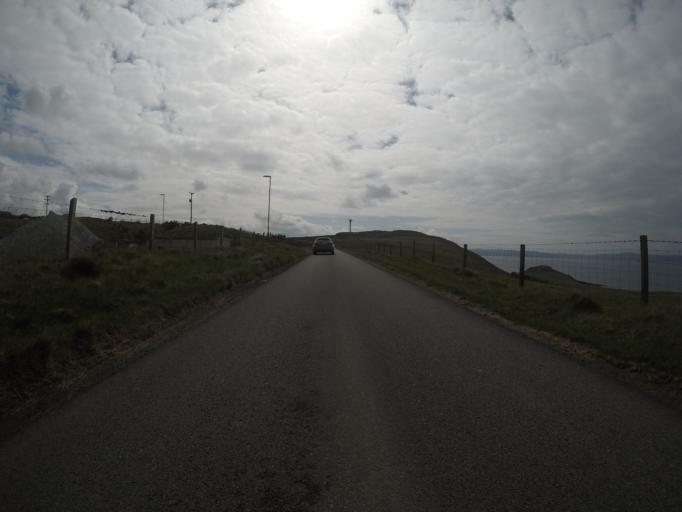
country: GB
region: Scotland
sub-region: Highland
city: Portree
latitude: 57.6031
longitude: -6.3775
